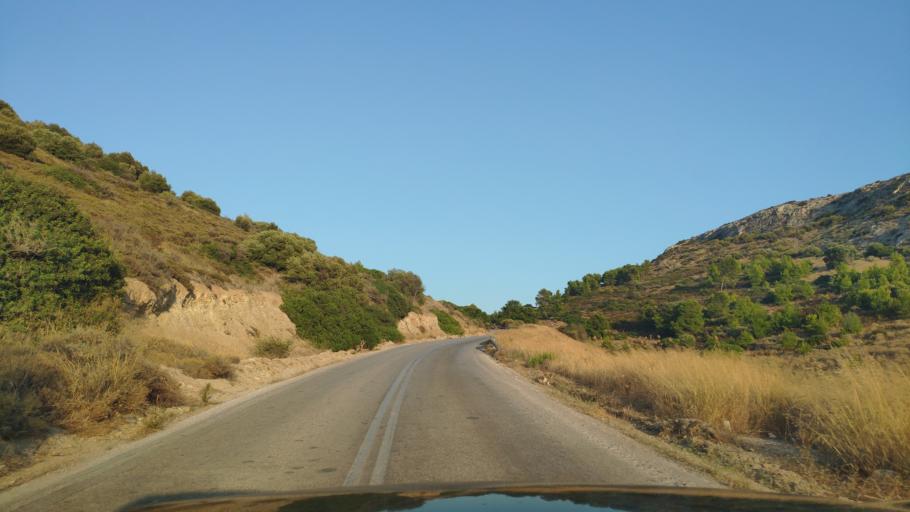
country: GR
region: Attica
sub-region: Nomarchia Anatolikis Attikis
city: Limin Mesoyaias
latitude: 37.9208
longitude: 24.0014
